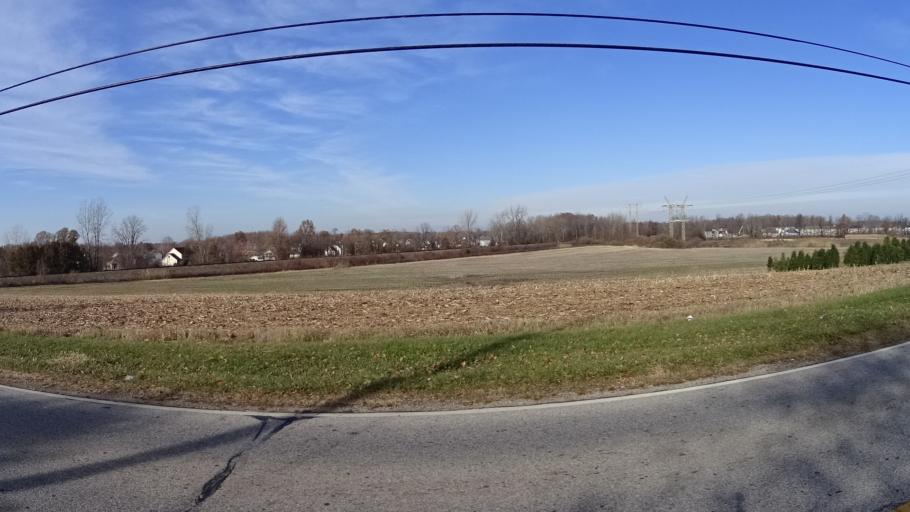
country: US
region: Ohio
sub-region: Lorain County
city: Sheffield
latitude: 41.4309
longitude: -82.0662
